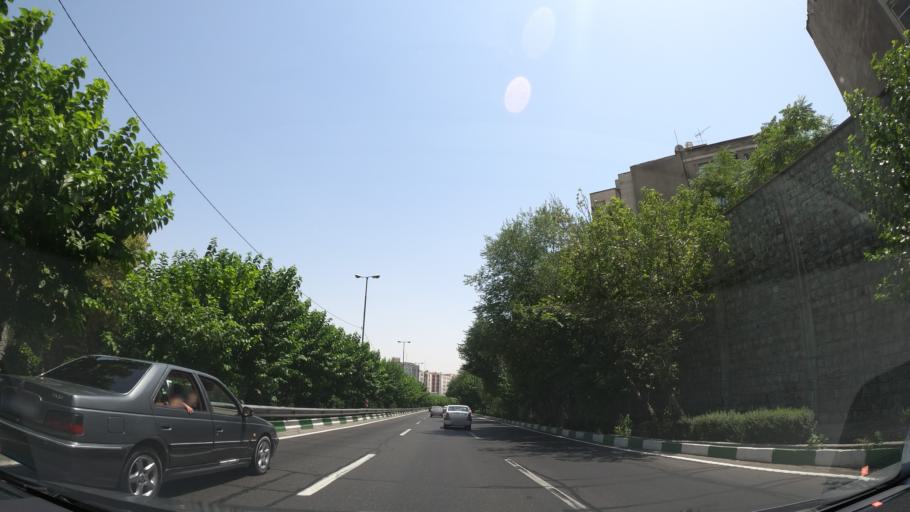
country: IR
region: Tehran
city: Tehran
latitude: 35.7284
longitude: 51.4222
